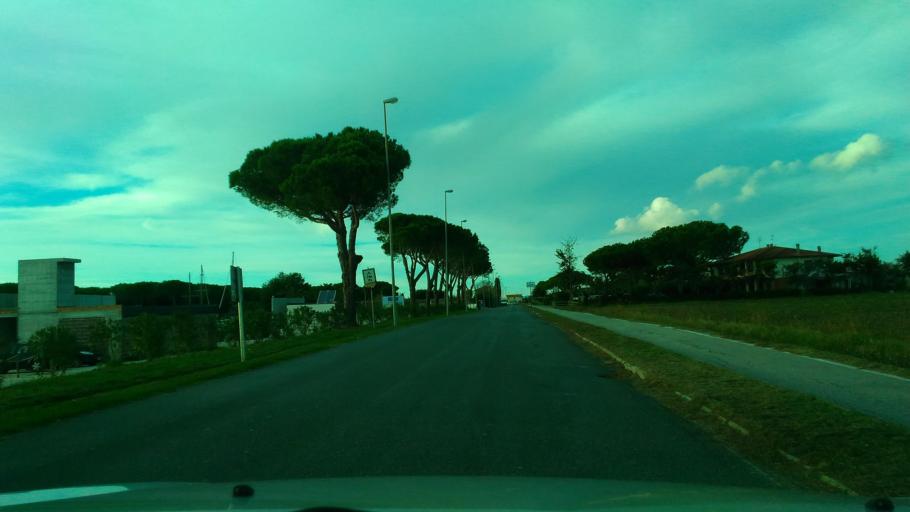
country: IT
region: Tuscany
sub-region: Provincia di Livorno
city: Cecina
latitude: 43.3064
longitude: 10.4911
